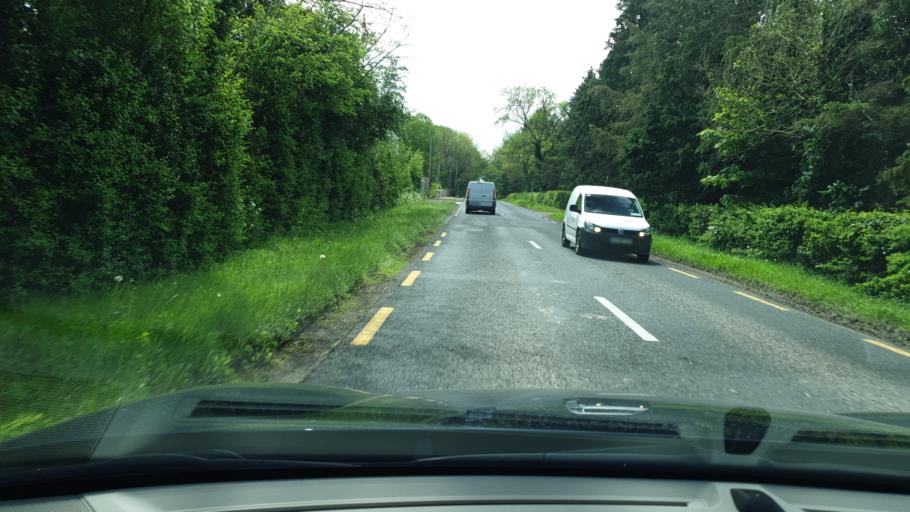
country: IE
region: Leinster
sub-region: An Mhi
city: Navan
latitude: 53.7463
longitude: -6.7177
